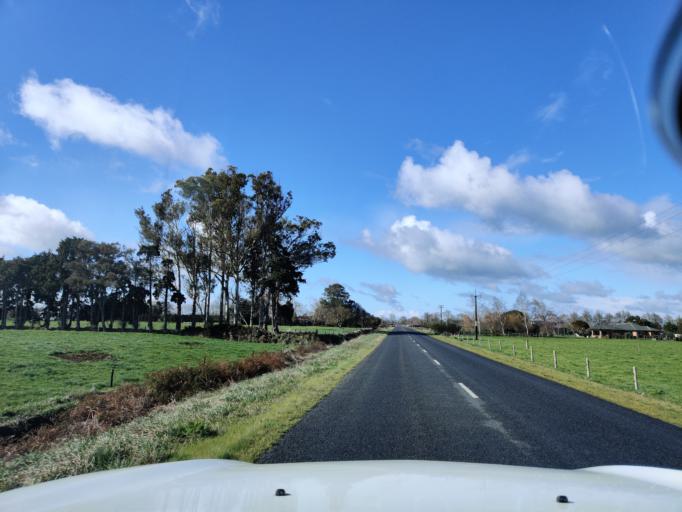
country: NZ
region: Waikato
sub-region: Waikato District
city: Ngaruawahia
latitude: -37.6024
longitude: 175.3019
